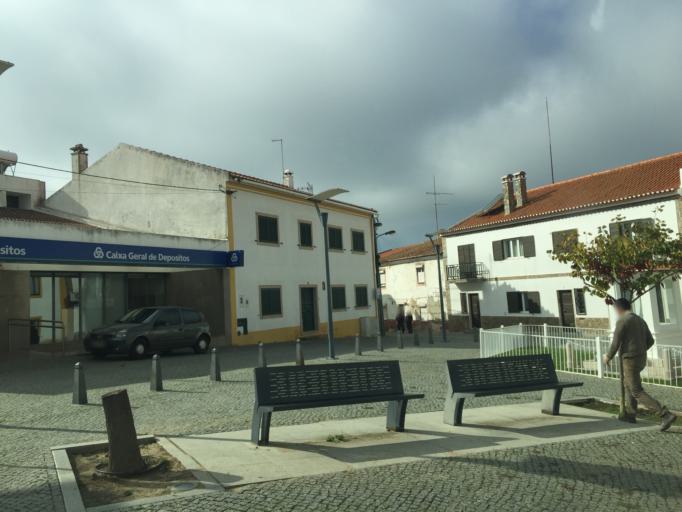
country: PT
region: Portalegre
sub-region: Fronteira
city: Fronteira
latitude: 39.0576
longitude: -7.6493
